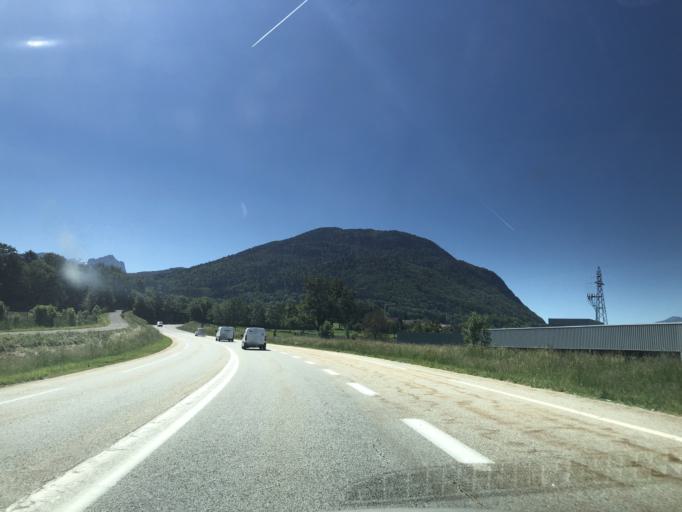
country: FR
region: Rhone-Alpes
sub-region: Departement de la Haute-Savoie
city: Villaz
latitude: 45.9315
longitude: 6.1715
